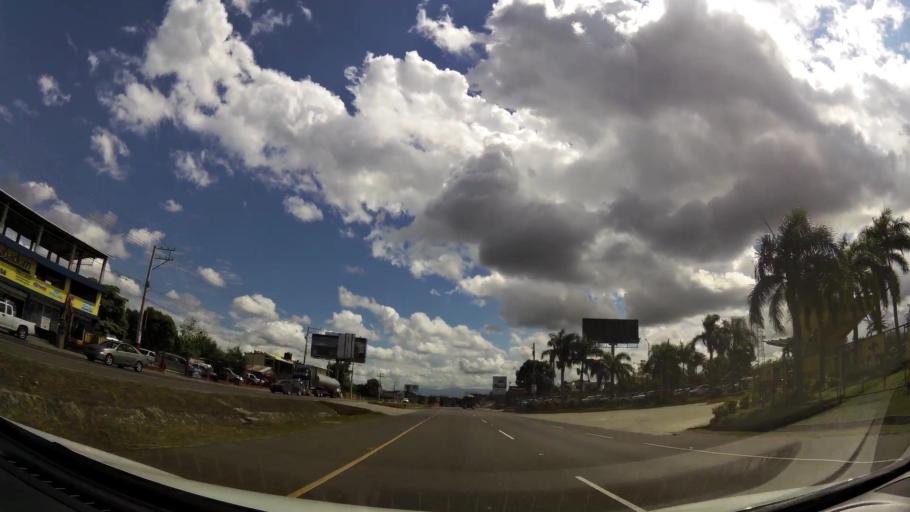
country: DO
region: Santiago
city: Licey al Medio
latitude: 19.3688
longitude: -70.6036
